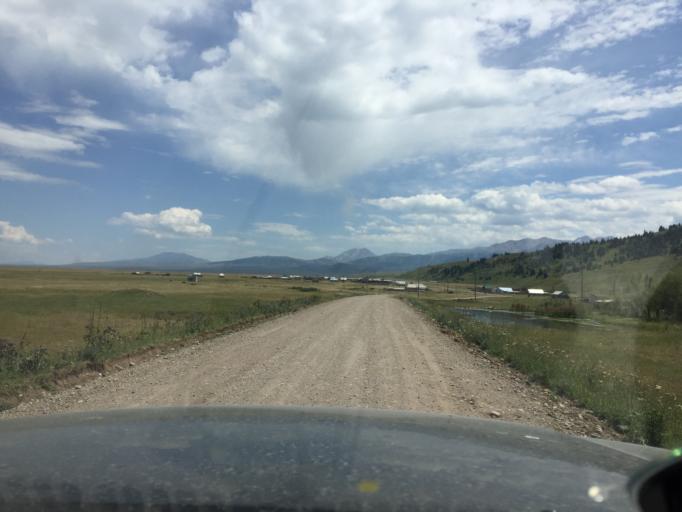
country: KZ
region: Almaty Oblysy
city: Kegen
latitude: 42.7607
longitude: 79.1362
